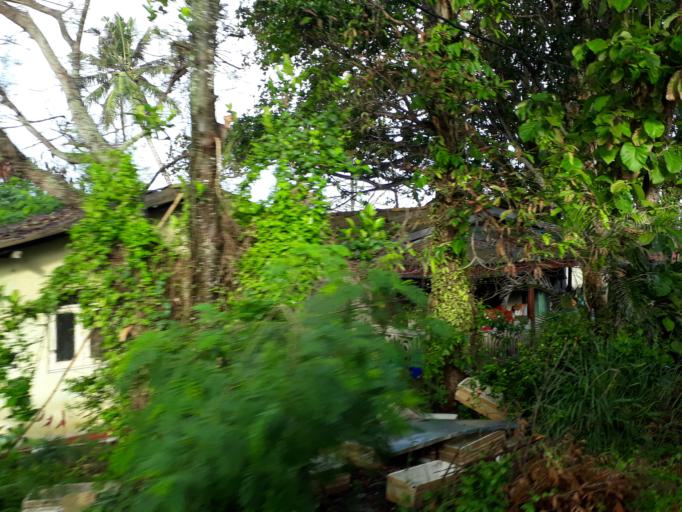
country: LK
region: Western
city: Kalutara
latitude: 6.5819
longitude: 79.9597
